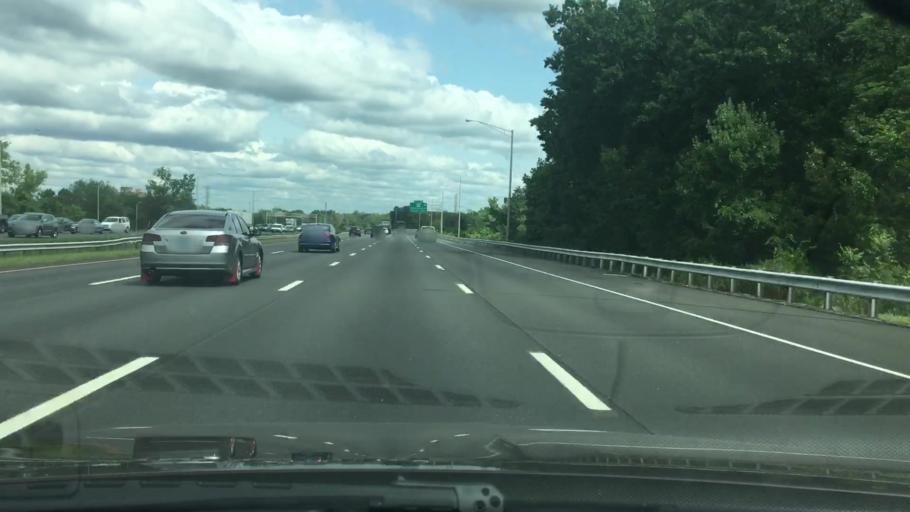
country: US
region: Connecticut
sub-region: Hartford County
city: Wethersfield
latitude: 41.6773
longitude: -72.6556
